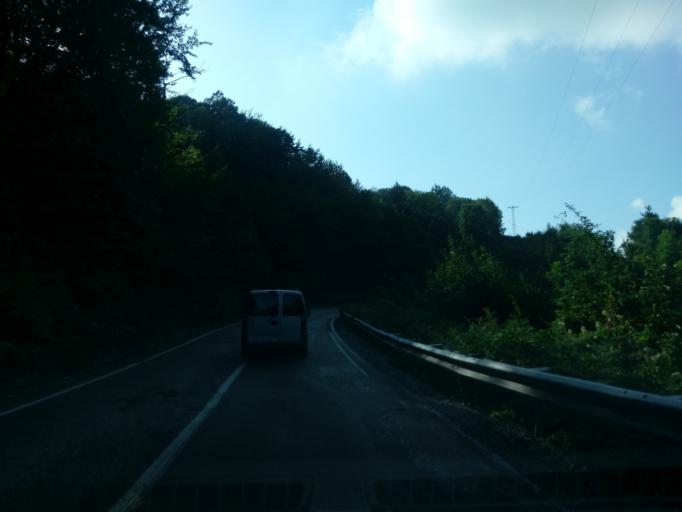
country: TR
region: Sinop
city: Ayancik
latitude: 41.8811
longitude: 34.5186
